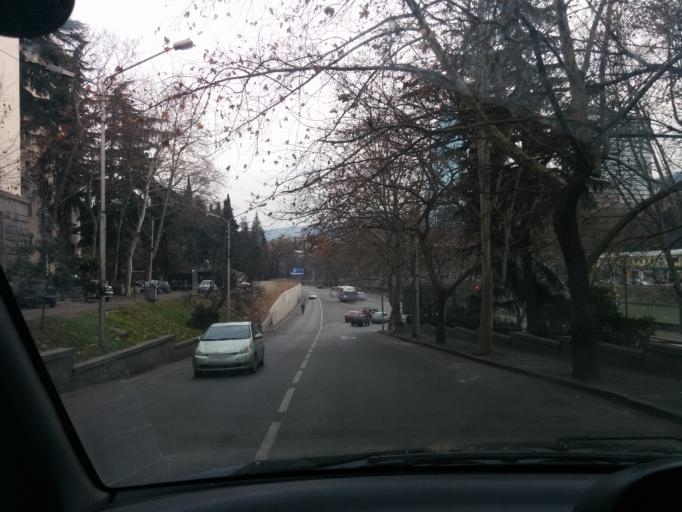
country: GE
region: T'bilisi
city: Tbilisi
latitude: 41.7079
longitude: 44.7938
